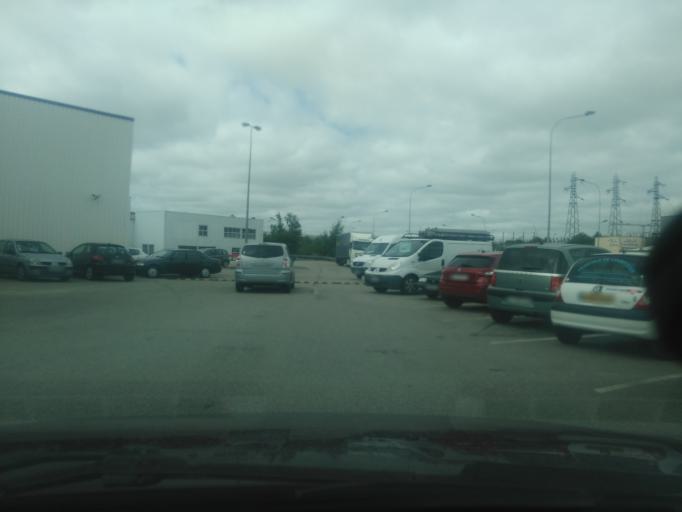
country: FR
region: Pays de la Loire
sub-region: Departement de la Vendee
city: La Roche-sur-Yon
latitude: 46.6896
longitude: -1.4313
